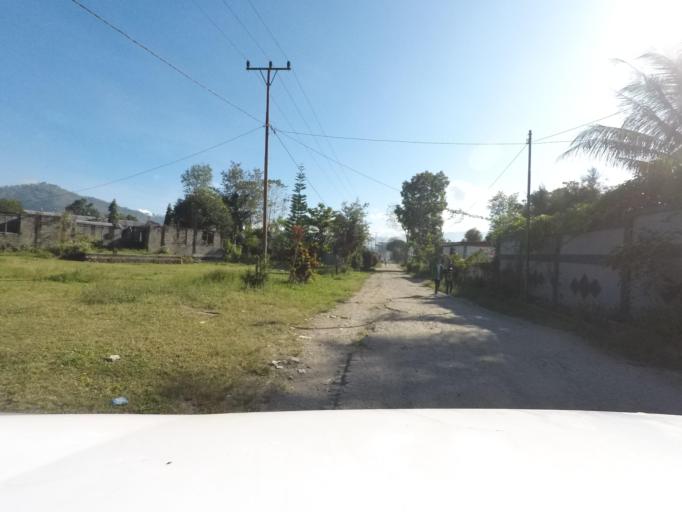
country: TL
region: Ermera
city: Gleno
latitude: -8.7264
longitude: 125.4307
